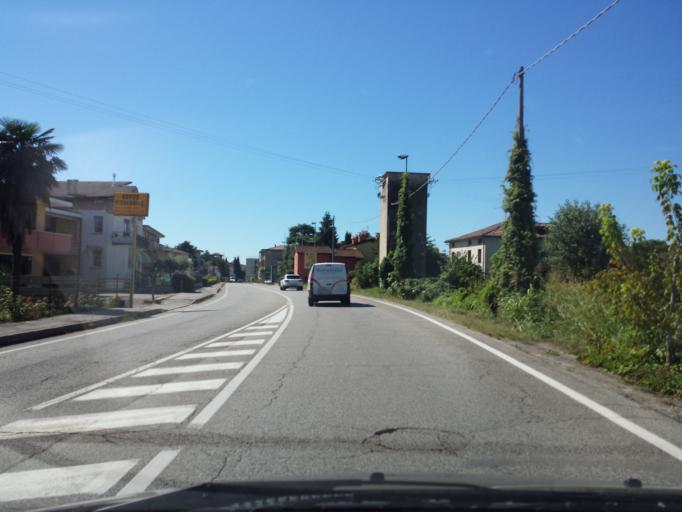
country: IT
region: Veneto
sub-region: Provincia di Vicenza
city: Dueville
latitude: 45.6307
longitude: 11.5708
